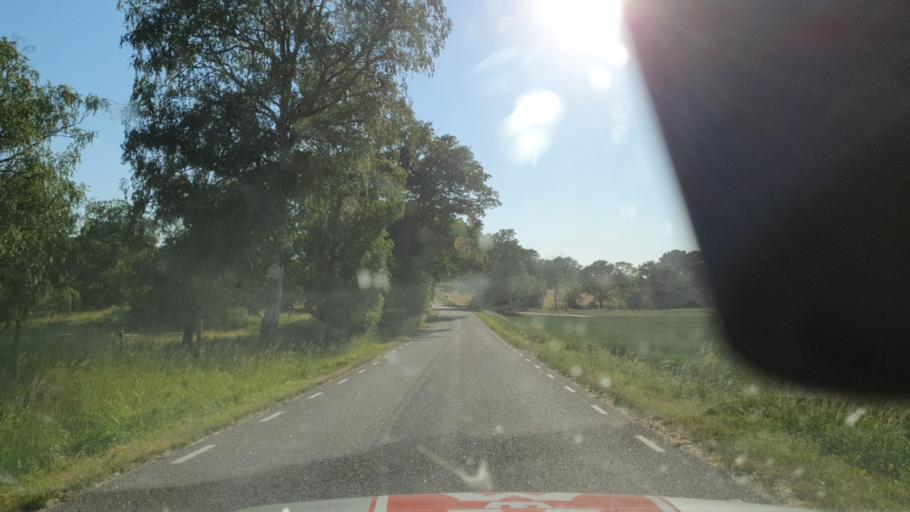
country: SE
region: Kalmar
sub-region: Kalmar Kommun
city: Ljungbyholm
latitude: 56.5008
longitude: 16.1148
